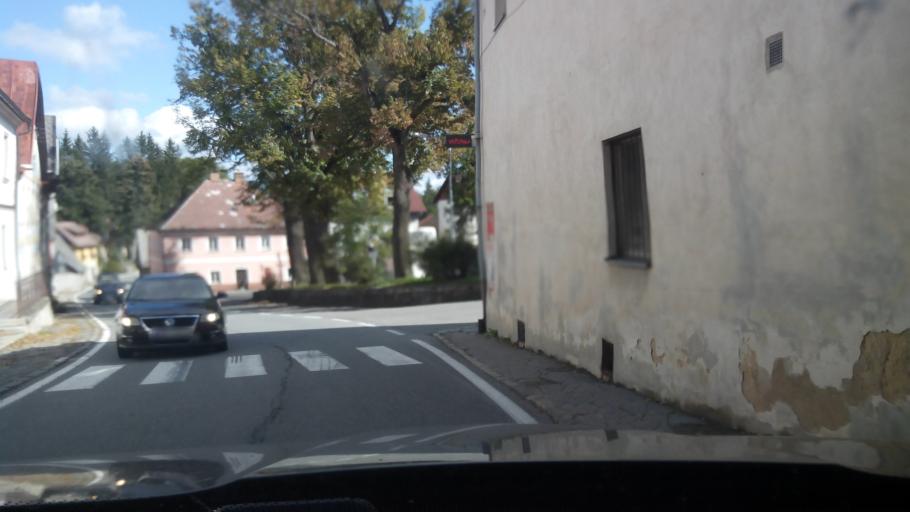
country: CZ
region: Jihocesky
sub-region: Okres Prachatice
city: Stachy
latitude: 49.1018
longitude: 13.6658
